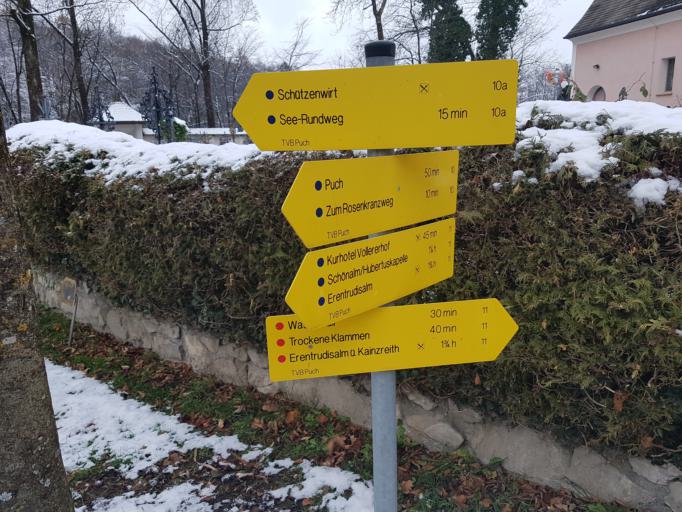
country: AT
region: Salzburg
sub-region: Politischer Bezirk Salzburg-Umgebung
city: Elsbethen
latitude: 47.7398
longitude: 13.0945
